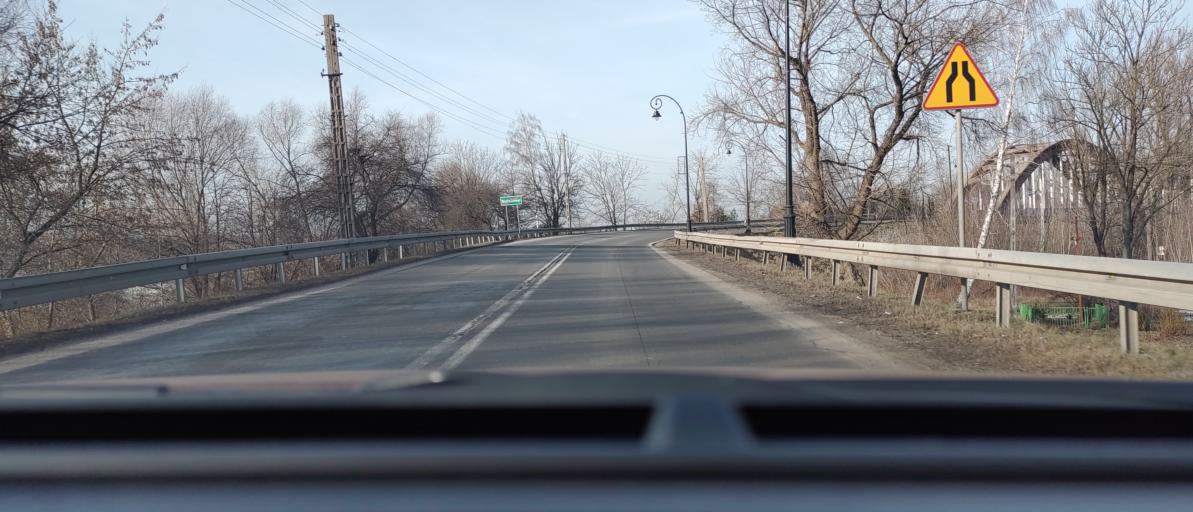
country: PL
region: Masovian Voivodeship
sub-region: Powiat bialobrzeski
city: Bialobrzegi
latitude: 51.6557
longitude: 20.9509
